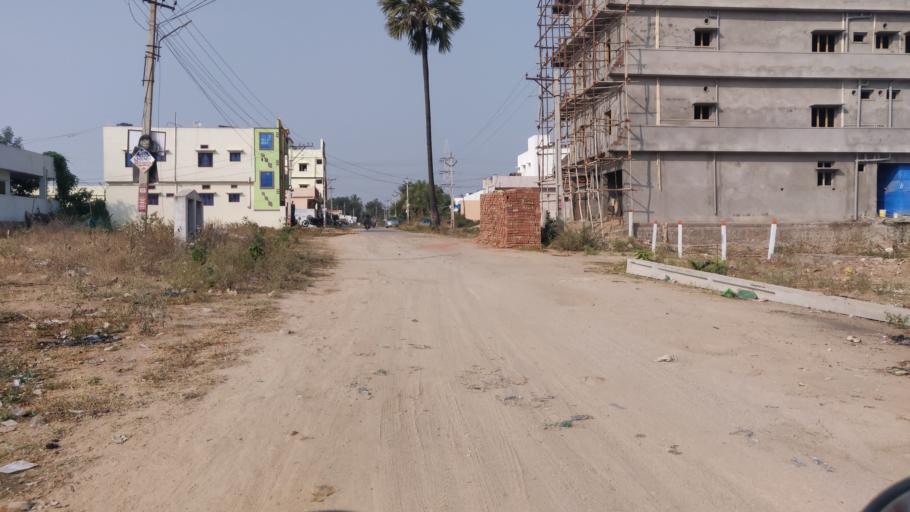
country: IN
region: Telangana
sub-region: Rangareddi
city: Uppal Kalan
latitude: 17.3949
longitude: 78.6050
